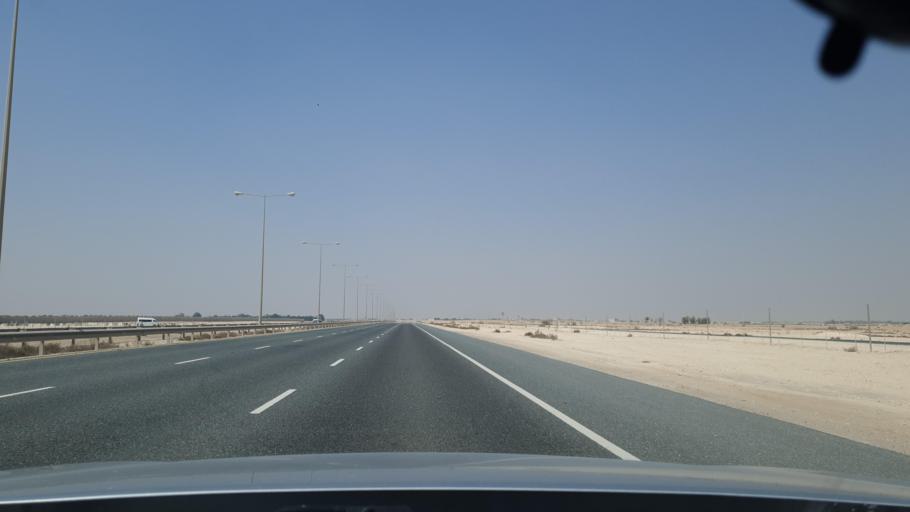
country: QA
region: Al Khawr
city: Al Khawr
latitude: 25.7674
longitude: 51.4173
